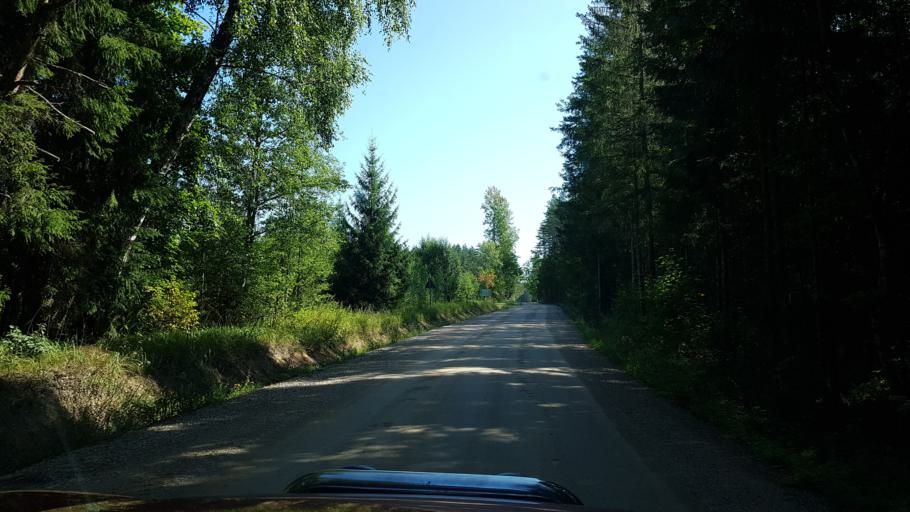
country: EE
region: Vorumaa
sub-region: Voru linn
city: Voru
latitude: 57.7349
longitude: 27.2194
